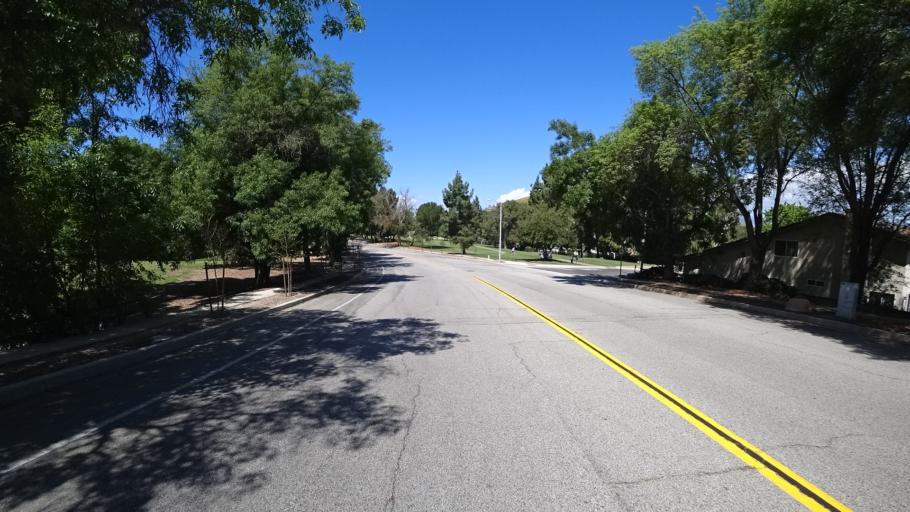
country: US
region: California
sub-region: Ventura County
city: Moorpark
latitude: 34.2364
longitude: -118.8437
